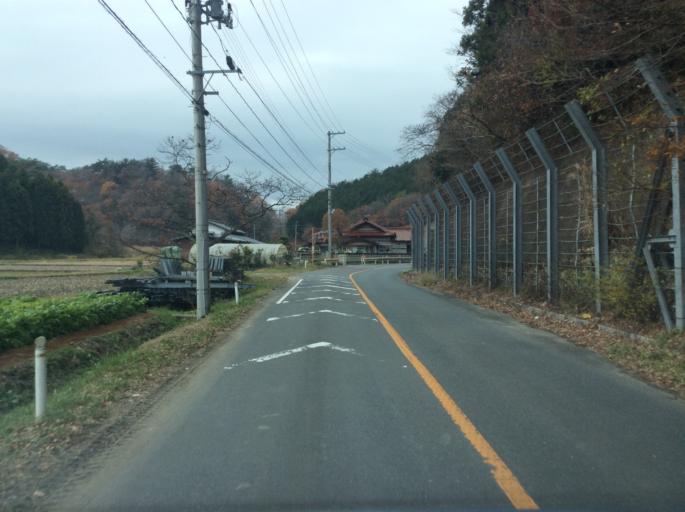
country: JP
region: Fukushima
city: Iwaki
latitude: 37.0477
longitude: 140.9270
